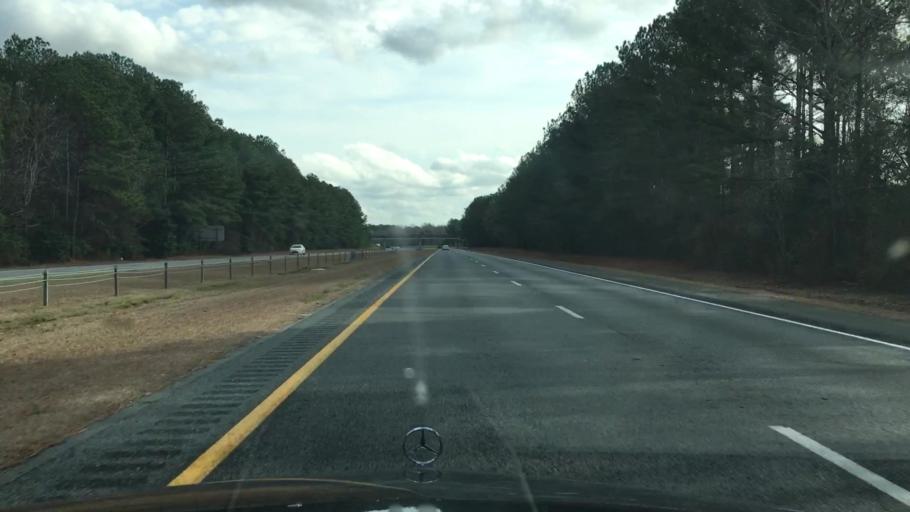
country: US
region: North Carolina
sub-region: Sampson County
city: Clinton
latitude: 35.2172
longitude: -78.3324
